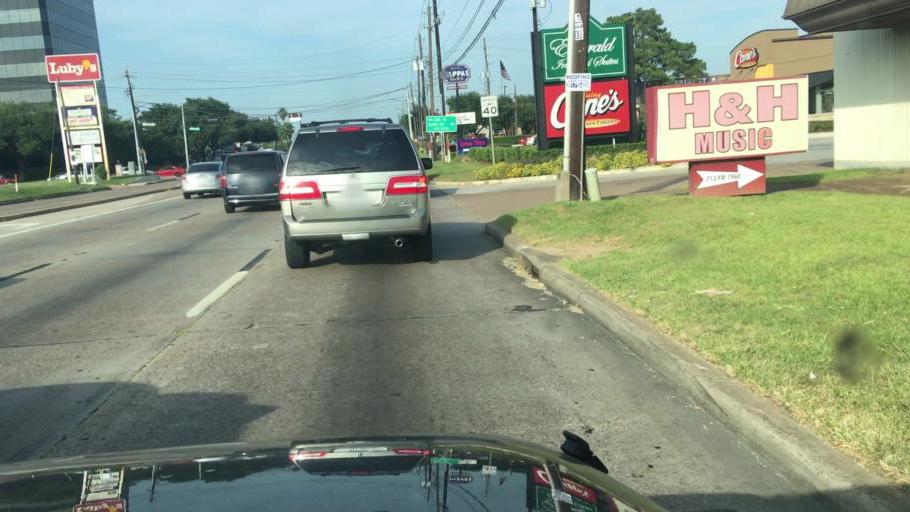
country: US
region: Texas
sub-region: Harris County
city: Spring
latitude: 30.0177
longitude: -95.4405
